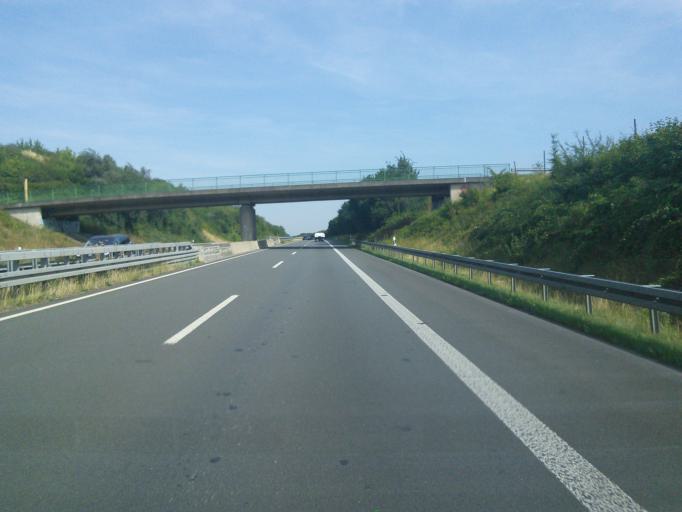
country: DE
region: North Rhine-Westphalia
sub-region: Regierungsbezirk Dusseldorf
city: Bruggen
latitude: 51.2094
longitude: 6.1418
